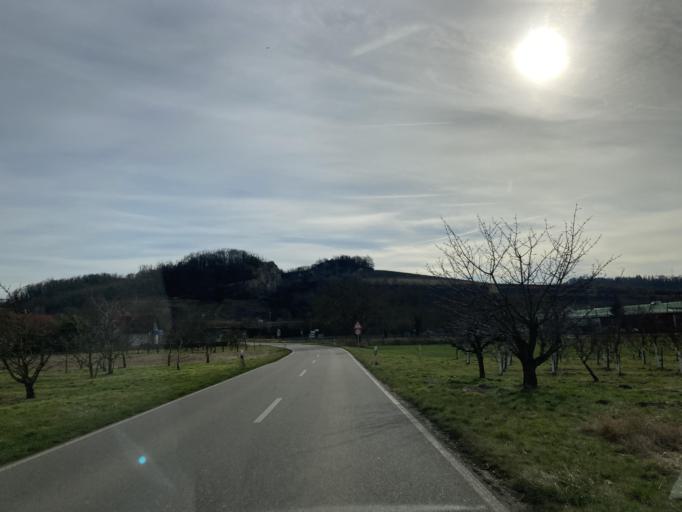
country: DE
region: Baden-Wuerttemberg
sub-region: Freiburg Region
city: Vogtsburg
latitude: 48.0849
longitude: 7.6071
